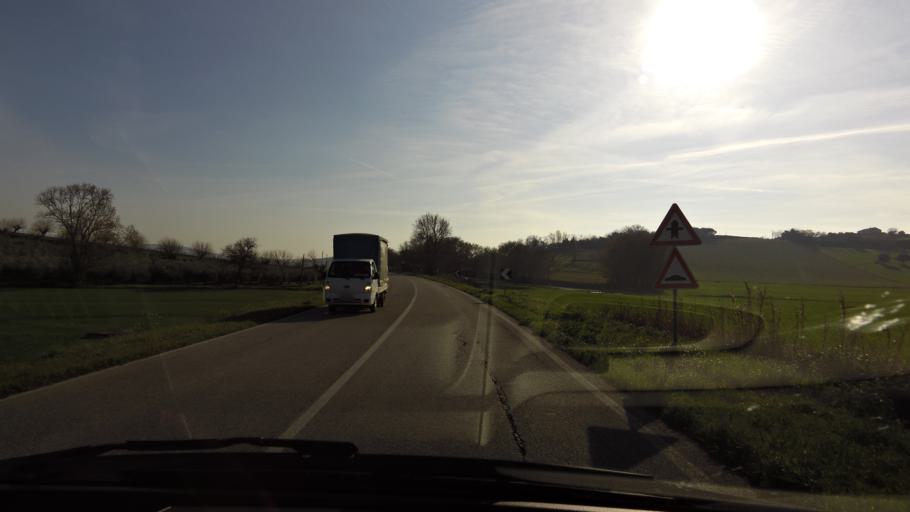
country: IT
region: The Marches
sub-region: Provincia di Ancona
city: Marcelli
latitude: 43.4865
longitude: 13.6079
